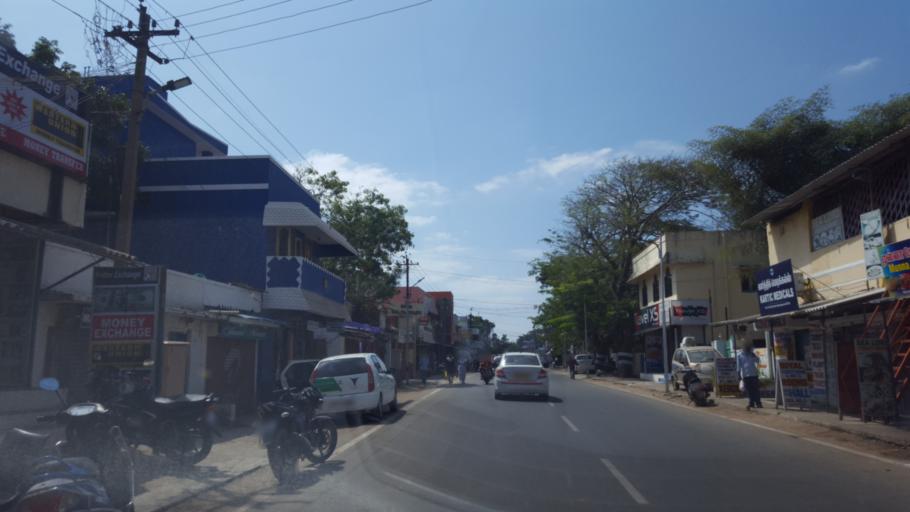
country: IN
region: Tamil Nadu
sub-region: Kancheepuram
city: Mamallapuram
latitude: 12.6199
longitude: 80.1944
